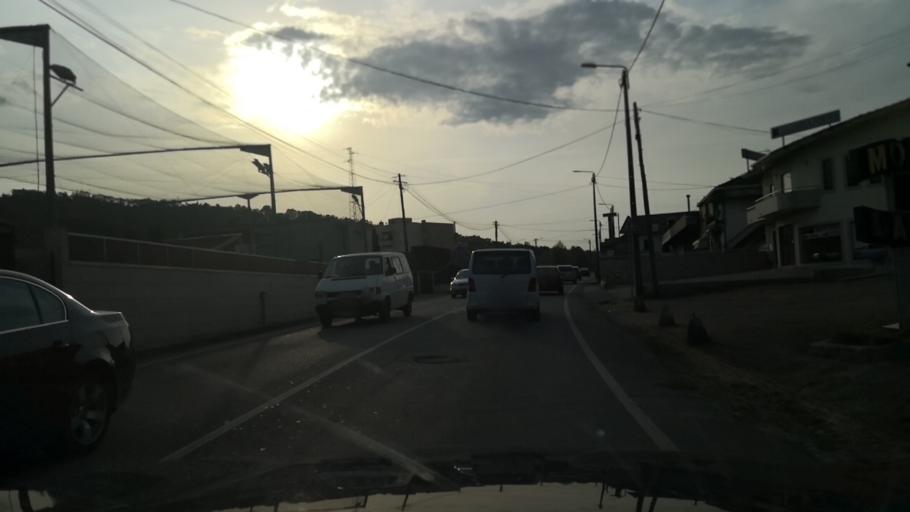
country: PT
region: Porto
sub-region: Valongo
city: Campo
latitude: 41.1821
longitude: -8.4771
